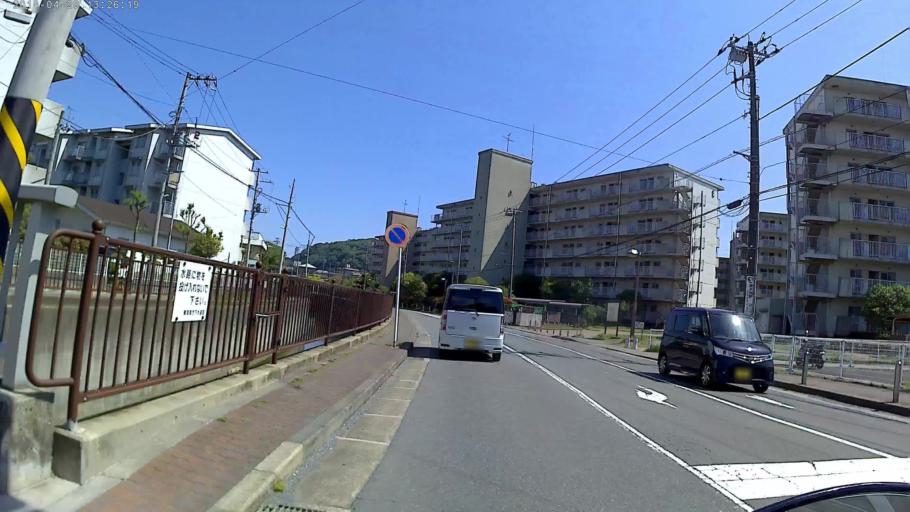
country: JP
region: Kanagawa
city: Yokosuka
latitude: 35.2282
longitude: 139.6983
